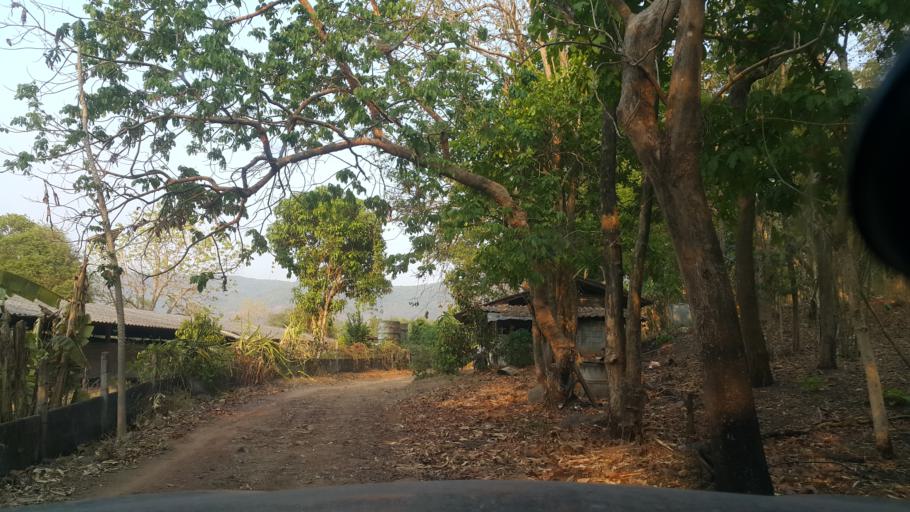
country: TH
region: Chiang Mai
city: Mae On
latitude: 18.7407
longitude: 99.2533
